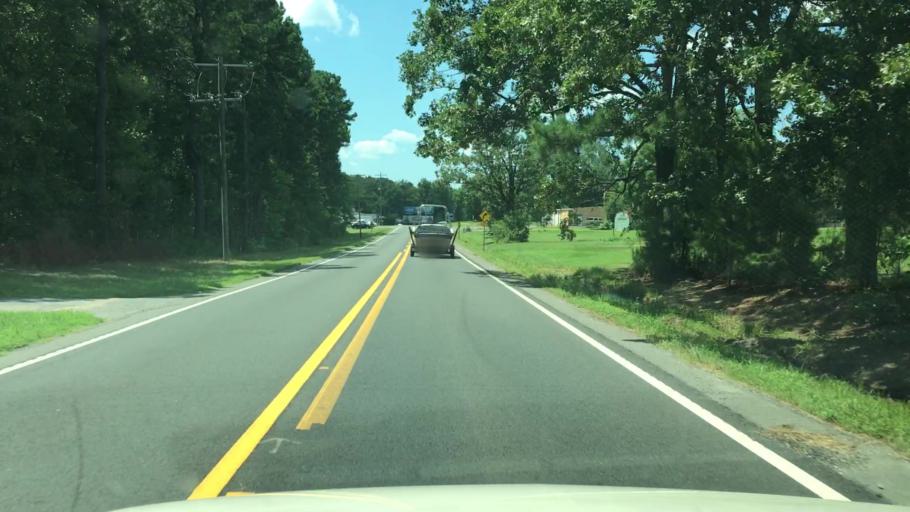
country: US
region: Arkansas
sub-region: Garland County
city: Lake Hamilton
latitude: 34.2673
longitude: -93.1413
